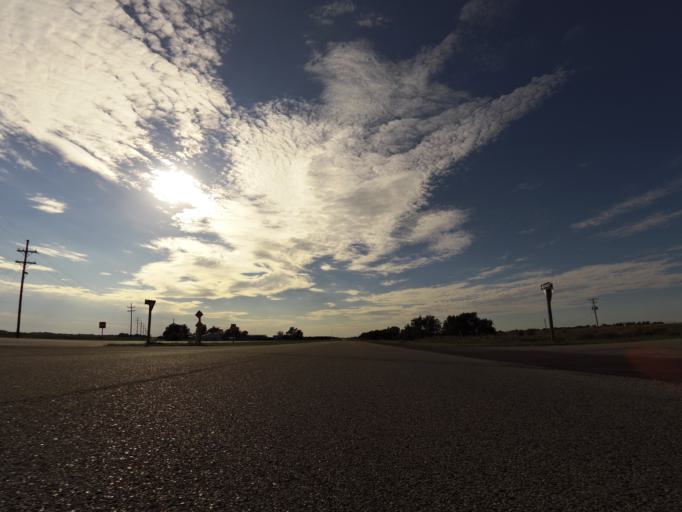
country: US
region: Kansas
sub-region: Reno County
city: South Hutchinson
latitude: 37.9555
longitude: -97.9029
